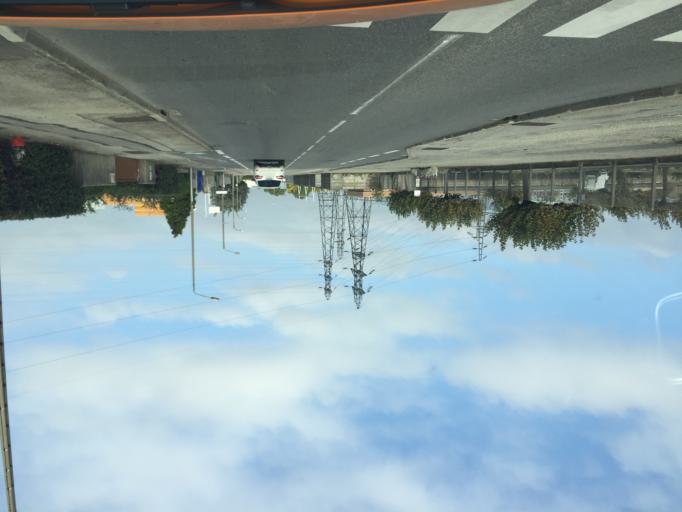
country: FR
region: Rhone-Alpes
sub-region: Departement de la Drome
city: Portes-les-Valence
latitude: 44.8886
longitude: 4.8851
